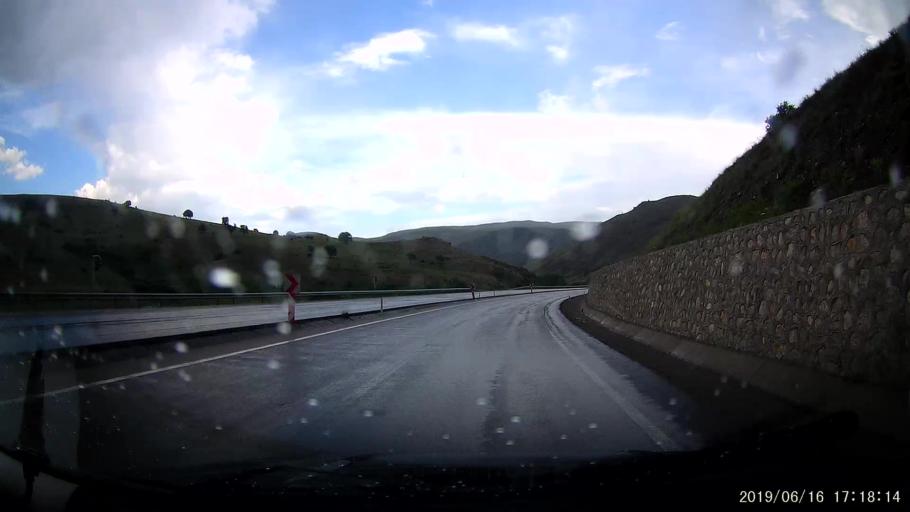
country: TR
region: Erzincan
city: Tercan
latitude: 39.8170
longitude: 40.5296
